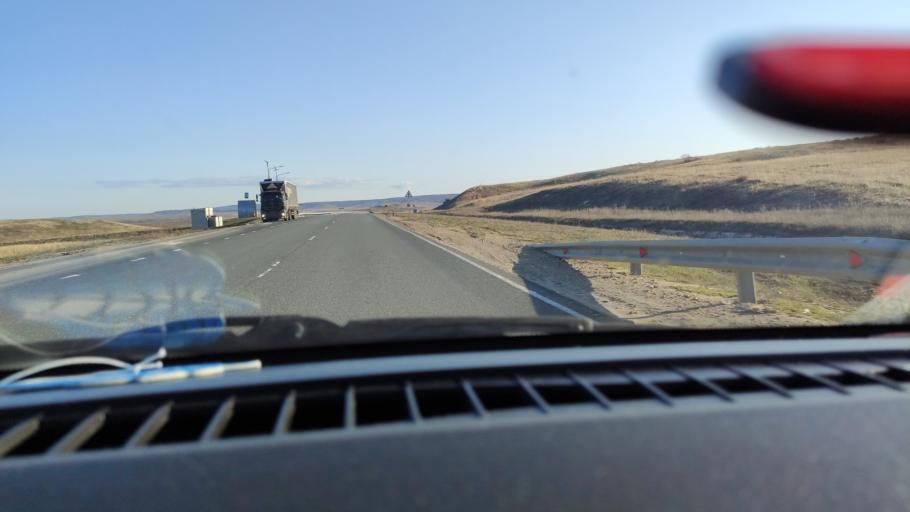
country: RU
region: Saratov
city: Alekseyevka
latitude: 52.3452
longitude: 47.9364
